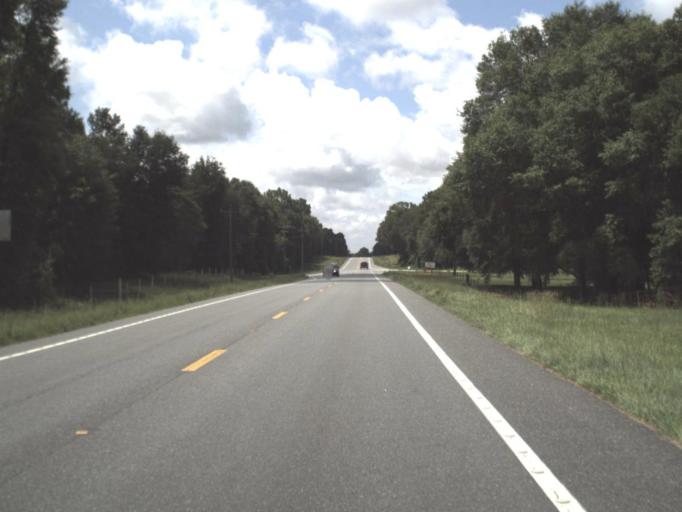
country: US
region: Florida
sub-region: Gilchrist County
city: Trenton
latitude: 29.8767
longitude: -82.8598
